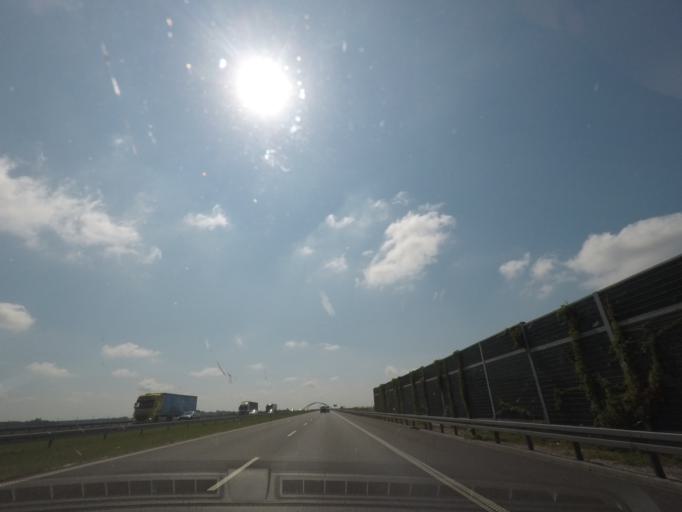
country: PL
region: Kujawsko-Pomorskie
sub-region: Powiat wloclawski
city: Chocen
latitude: 52.5772
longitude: 19.0014
